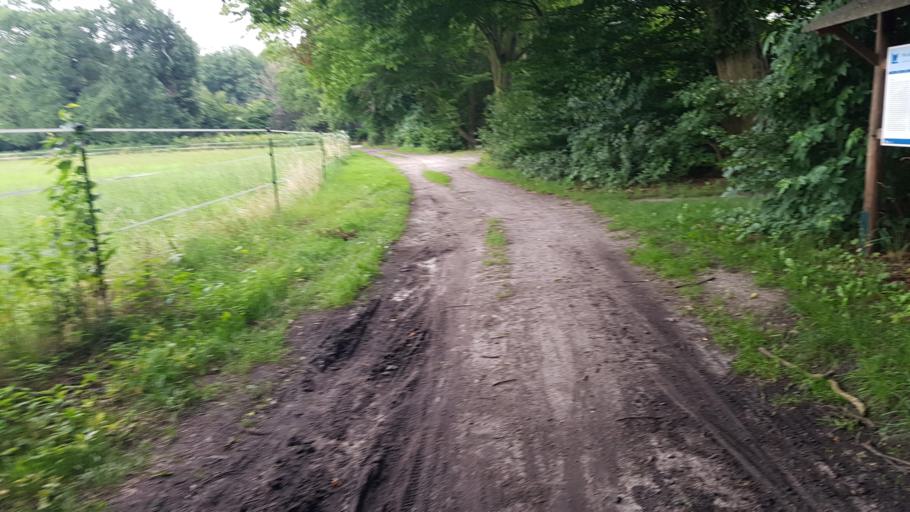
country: DE
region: Brandenburg
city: Sonnewalde
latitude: 51.6964
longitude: 13.6392
